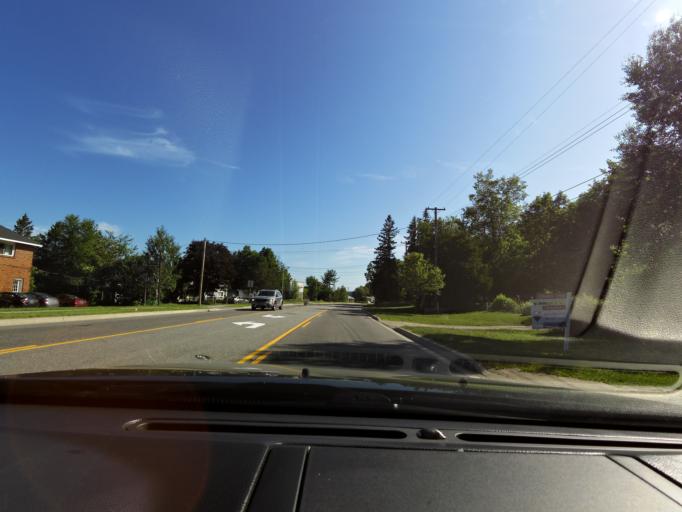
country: CA
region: Ontario
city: Huntsville
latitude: 45.3175
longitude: -79.2390
